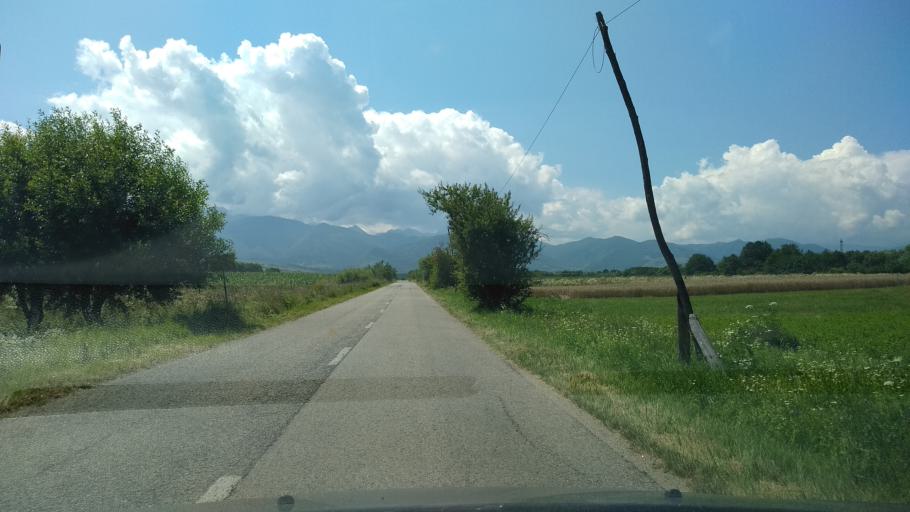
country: RO
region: Hunedoara
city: Salasu de Sus
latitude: 45.5288
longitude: 22.9668
